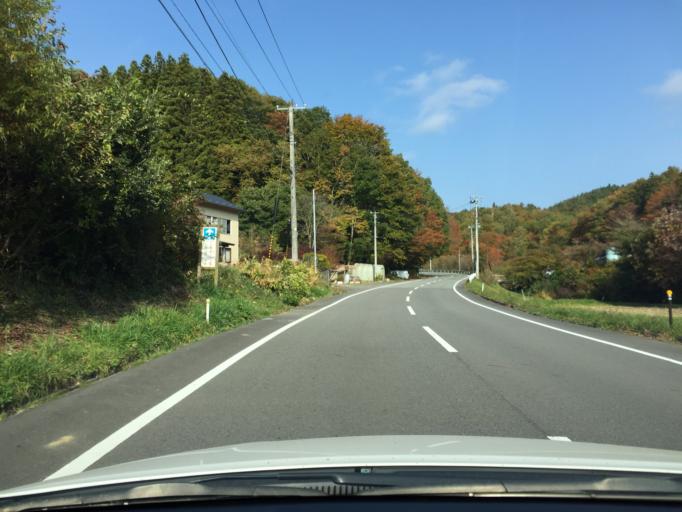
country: JP
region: Ibaraki
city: Kitaibaraki
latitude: 36.9549
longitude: 140.5916
